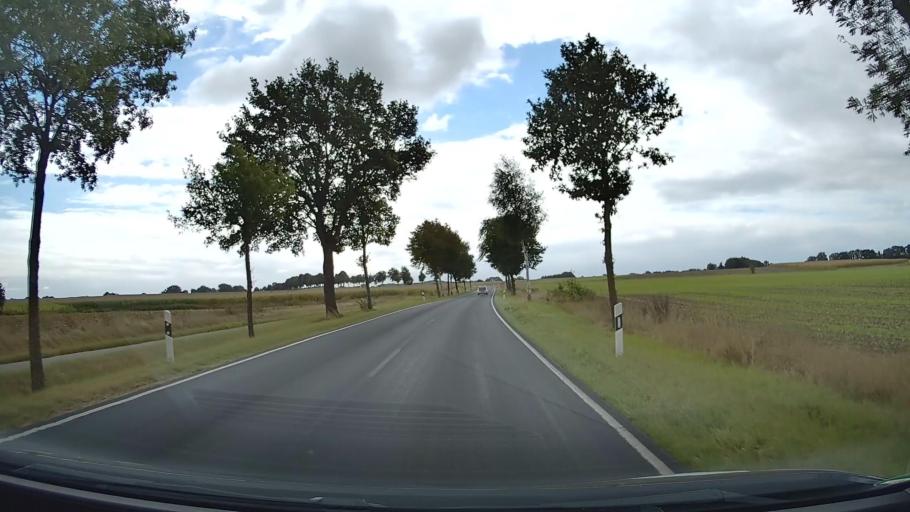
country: DE
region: Lower Saxony
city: Rhade
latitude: 53.3211
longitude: 9.1262
